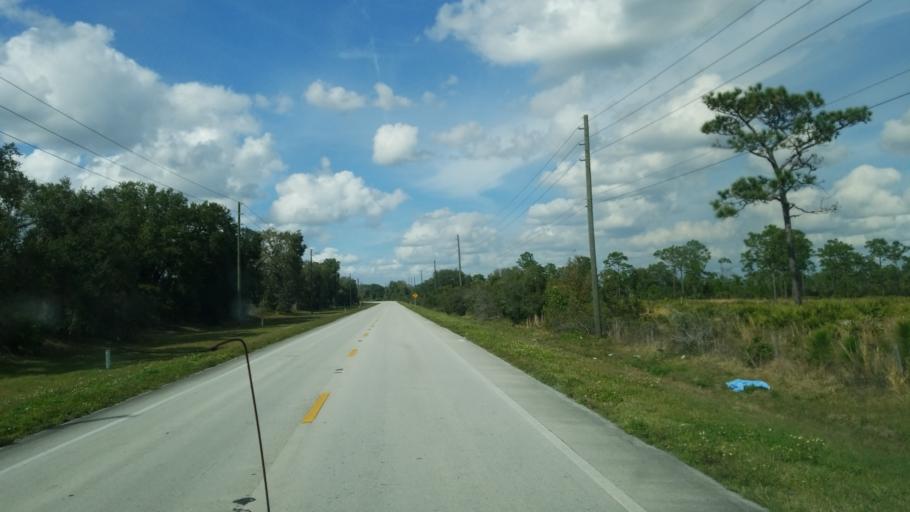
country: US
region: Florida
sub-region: Osceola County
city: Saint Cloud
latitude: 28.0871
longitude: -81.0725
